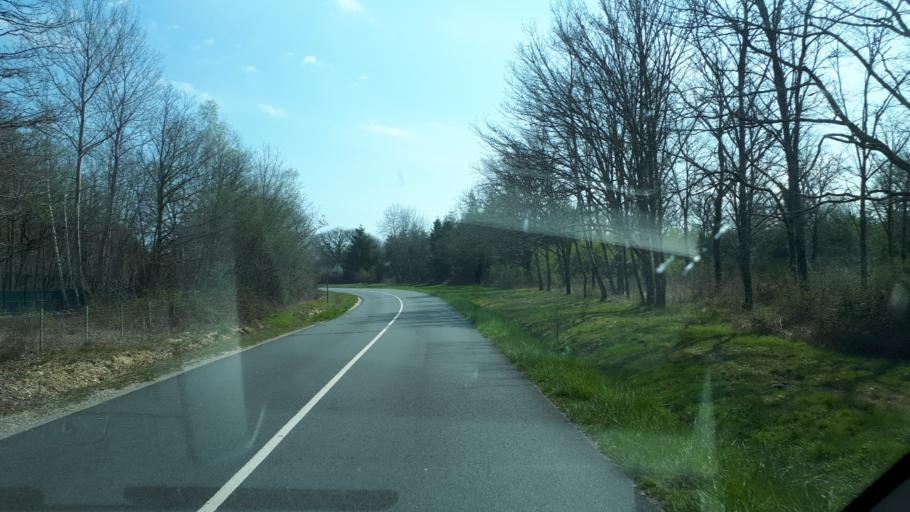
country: FR
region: Centre
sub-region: Departement du Loir-et-Cher
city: Selles-Saint-Denis
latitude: 47.3384
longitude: 1.9197
